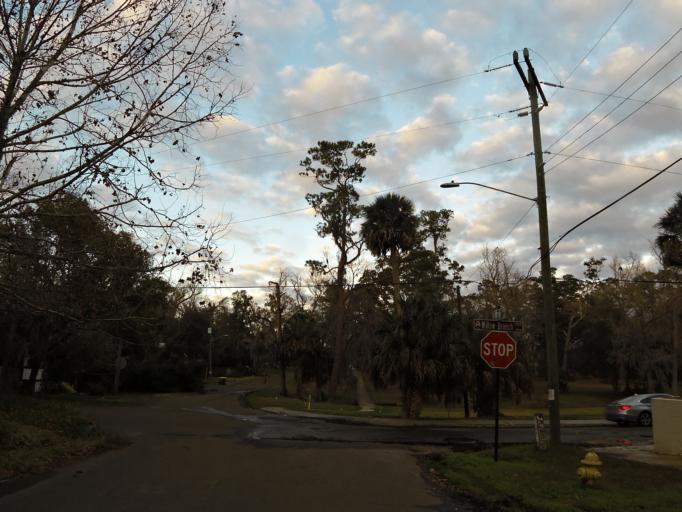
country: US
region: Florida
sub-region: Duval County
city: Jacksonville
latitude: 30.3068
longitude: -81.7011
